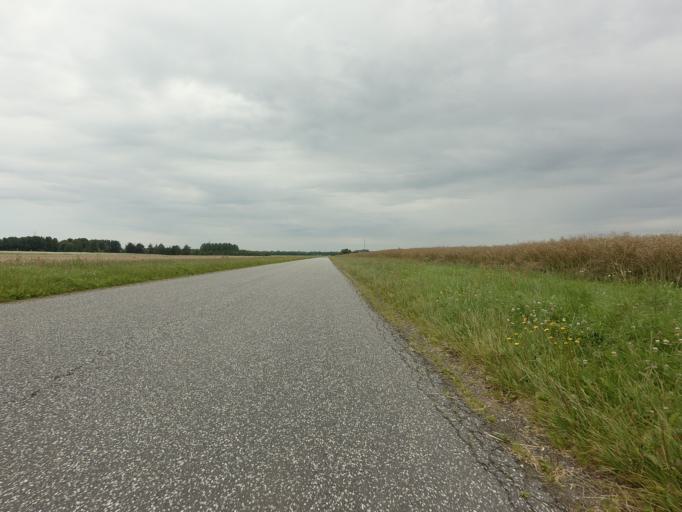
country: DK
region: North Denmark
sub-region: Alborg Kommune
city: Vadum
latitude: 57.1266
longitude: 9.8535
